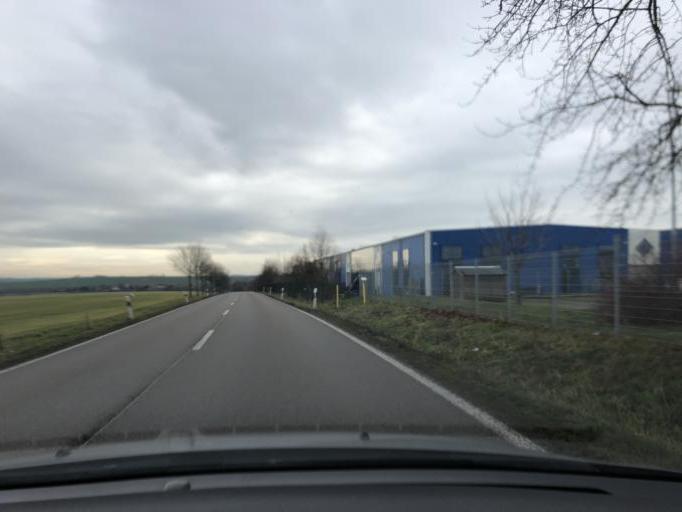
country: DE
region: Saxony
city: Nossen
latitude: 51.0668
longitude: 13.3393
